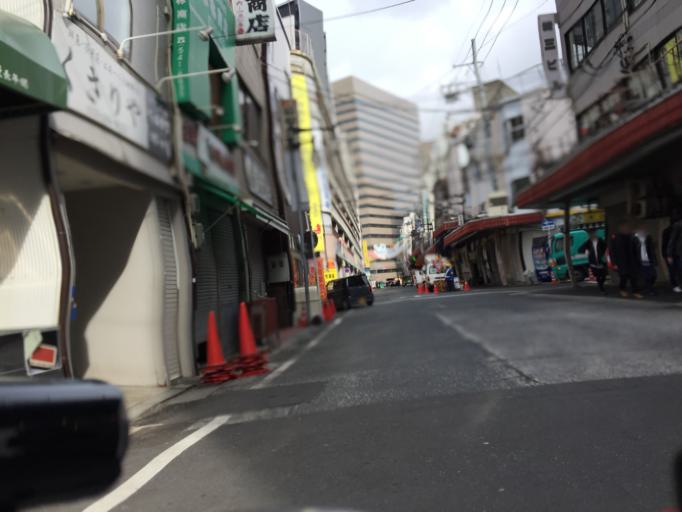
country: JP
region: Aichi
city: Nagoya-shi
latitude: 35.1693
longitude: 136.8881
